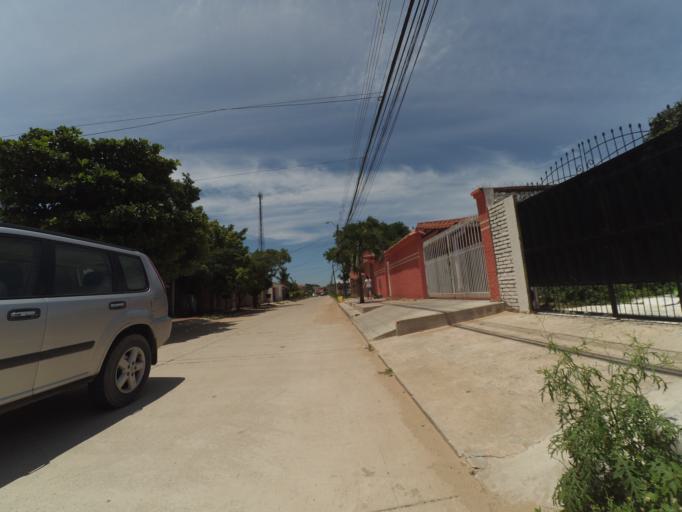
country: BO
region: Santa Cruz
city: Santa Cruz de la Sierra
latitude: -17.8127
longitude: -63.2238
